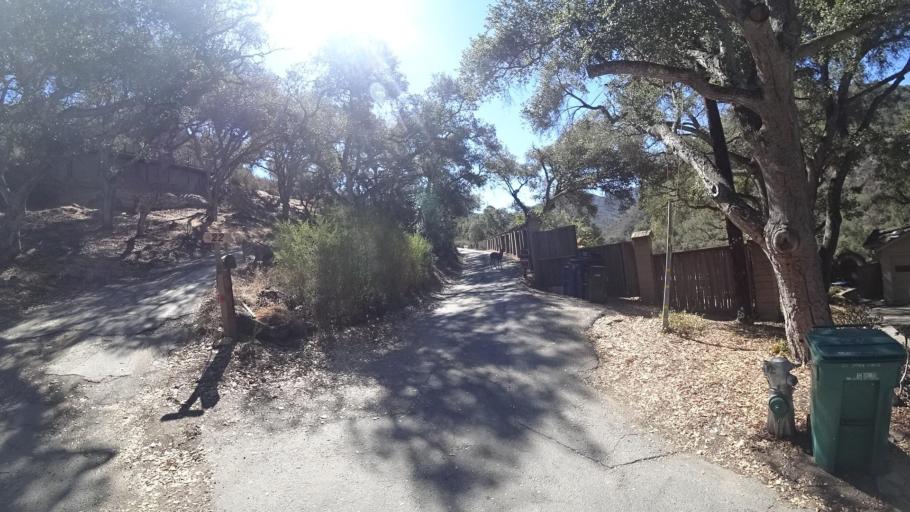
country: US
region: California
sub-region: Monterey County
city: Carmel Valley Village
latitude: 36.4696
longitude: -121.7229
